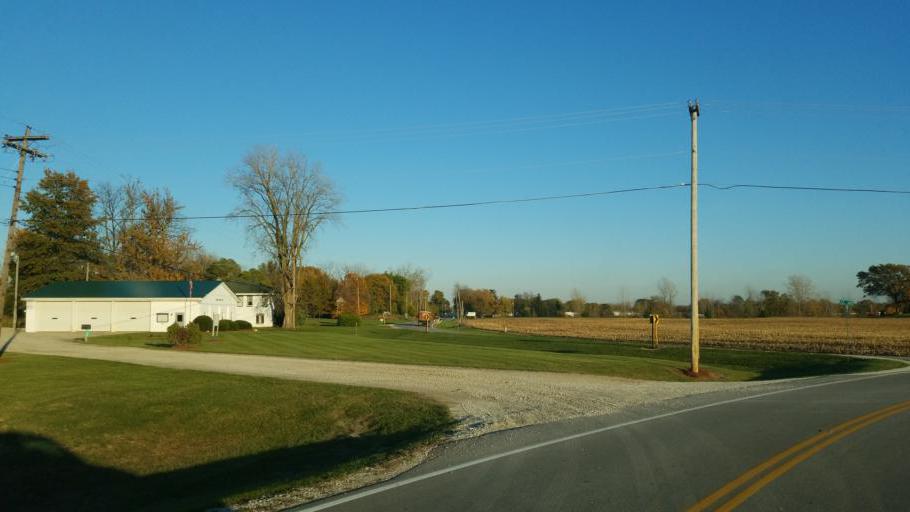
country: US
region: Ohio
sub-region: Sandusky County
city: Clyde
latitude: 41.2924
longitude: -83.0142
